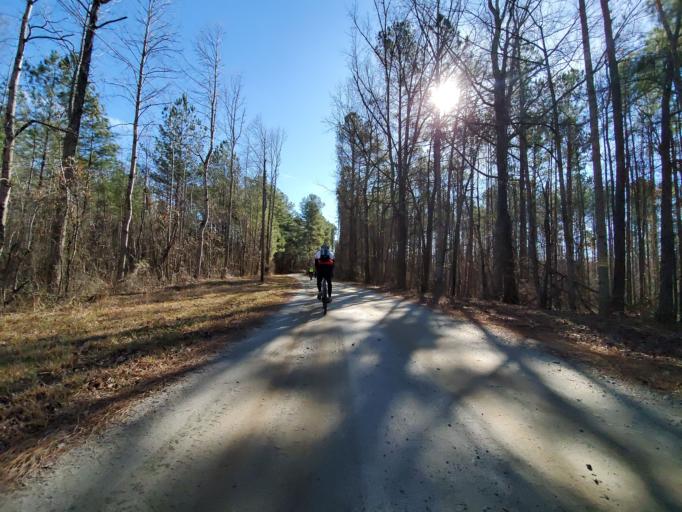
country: US
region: Georgia
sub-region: Fulton County
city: Chattahoochee Hills
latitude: 33.5812
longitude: -84.7899
